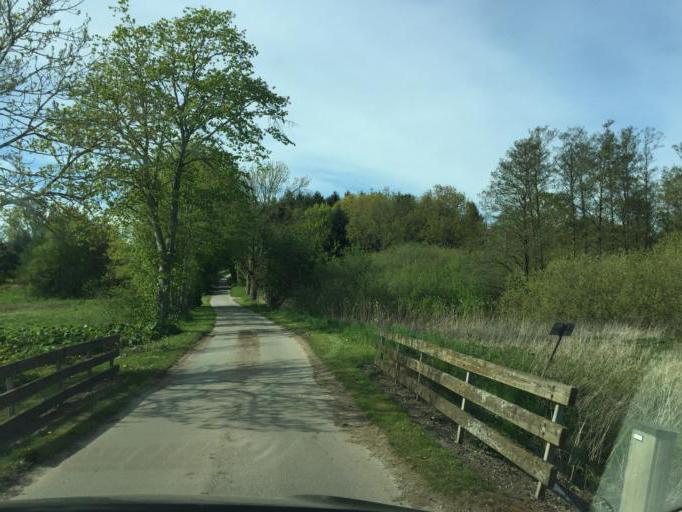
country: DK
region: South Denmark
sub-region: Fredericia Kommune
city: Taulov
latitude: 55.5341
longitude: 9.5648
